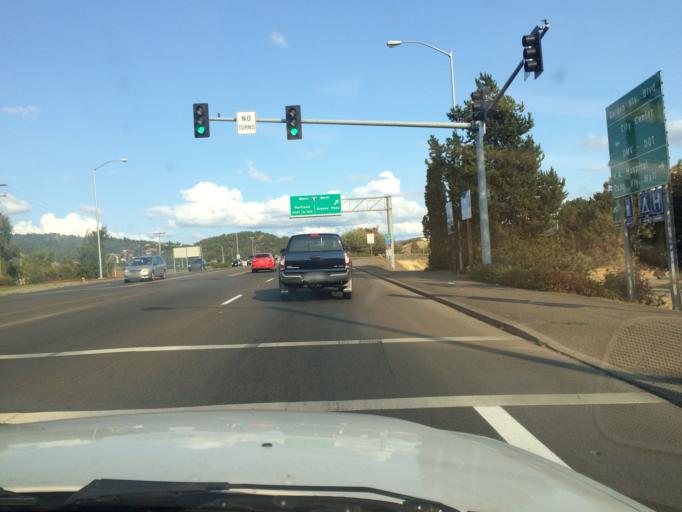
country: US
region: Oregon
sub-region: Douglas County
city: Roseburg
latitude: 43.2276
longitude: -123.3639
